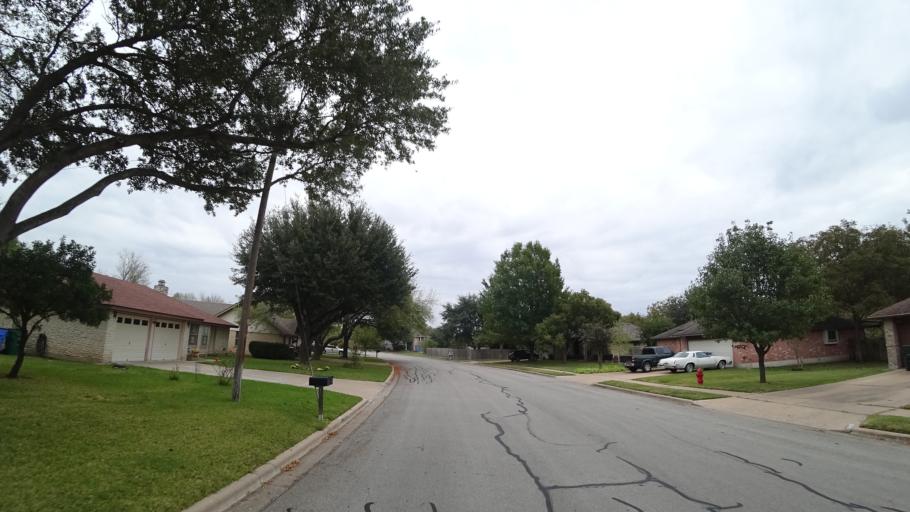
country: US
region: Texas
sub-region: Travis County
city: Pflugerville
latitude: 30.4466
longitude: -97.6195
